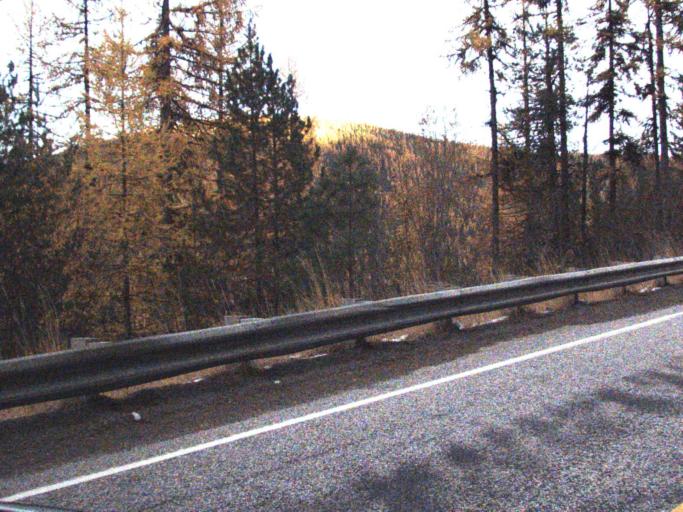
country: US
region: Washington
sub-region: Ferry County
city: Republic
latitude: 48.6126
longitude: -118.4437
